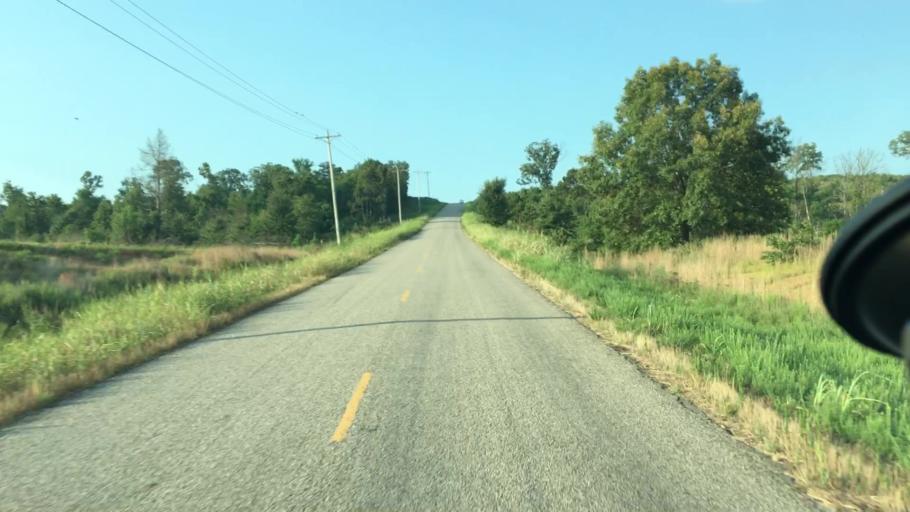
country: US
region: Arkansas
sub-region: Johnson County
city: Coal Hill
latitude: 35.3605
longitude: -93.6131
